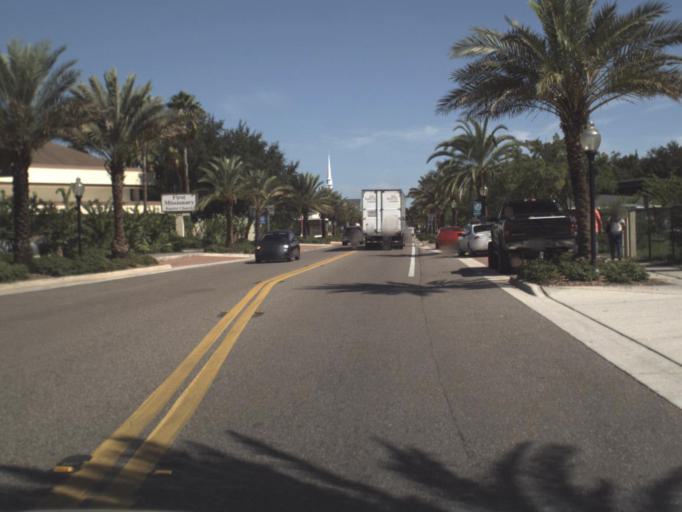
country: US
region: Florida
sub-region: Polk County
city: Auburndale
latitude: 28.0594
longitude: -81.7886
